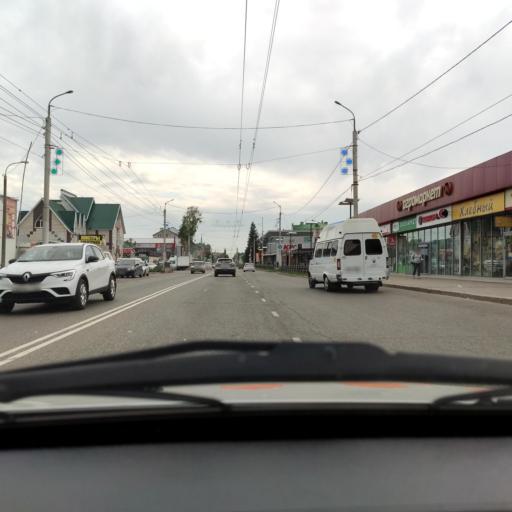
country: RU
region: Bashkortostan
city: Sterlitamak
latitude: 53.6131
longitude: 55.9547
